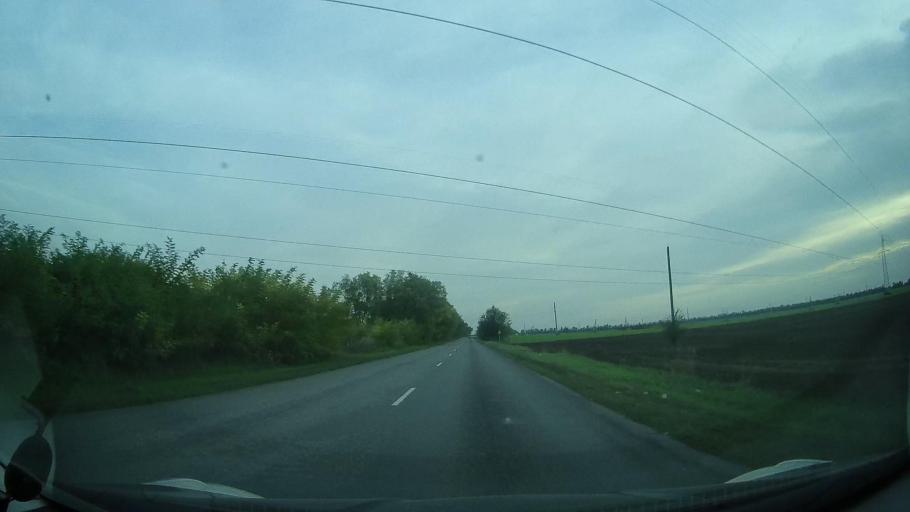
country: RU
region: Rostov
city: Ol'ginskaya
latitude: 47.1113
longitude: 39.9774
